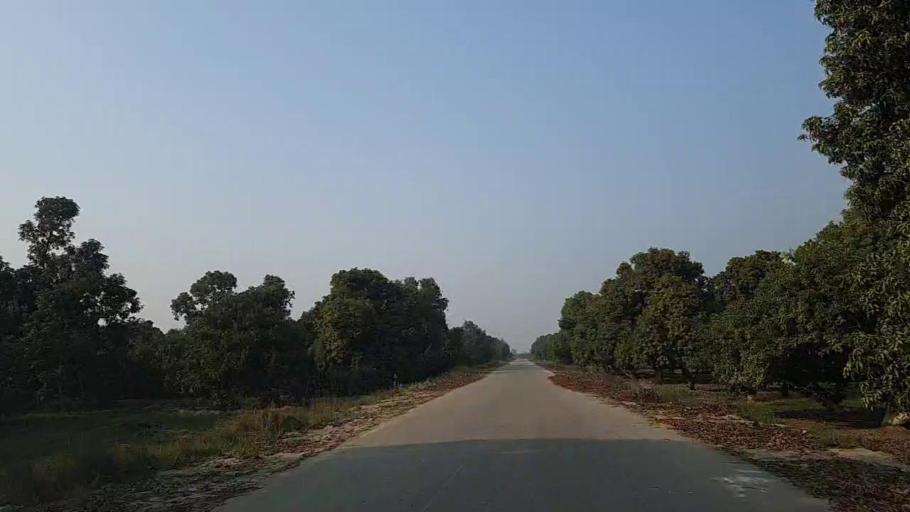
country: PK
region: Sindh
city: Sann
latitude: 26.1064
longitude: 68.1510
